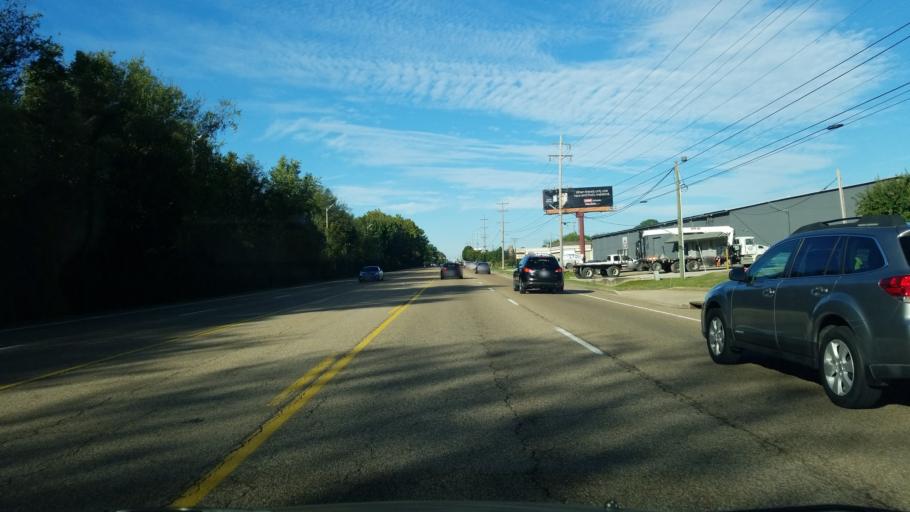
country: US
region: Tennessee
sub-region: Hamilton County
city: East Chattanooga
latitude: 35.0667
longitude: -85.2722
